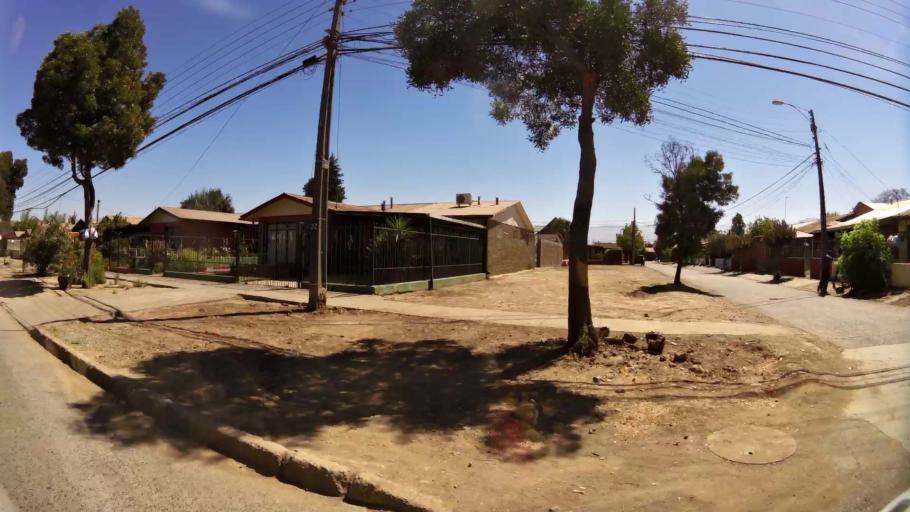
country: CL
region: O'Higgins
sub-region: Provincia de Cachapoal
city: Rancagua
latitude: -34.1773
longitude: -70.7160
